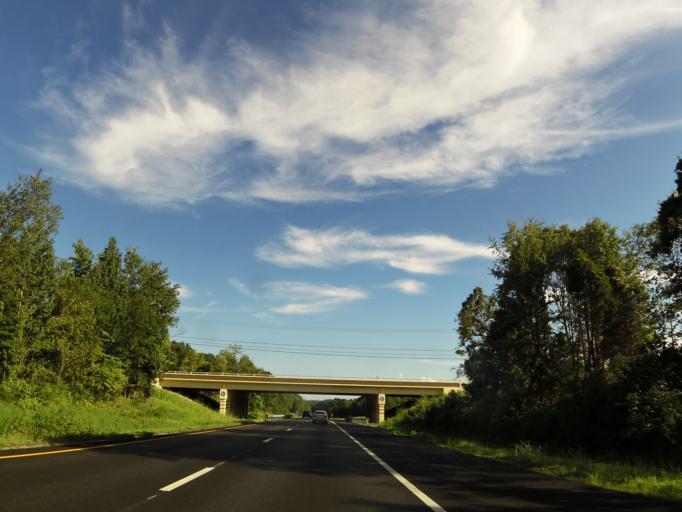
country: US
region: Tennessee
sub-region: Montgomery County
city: Clarksville
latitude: 36.5570
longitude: -87.2507
